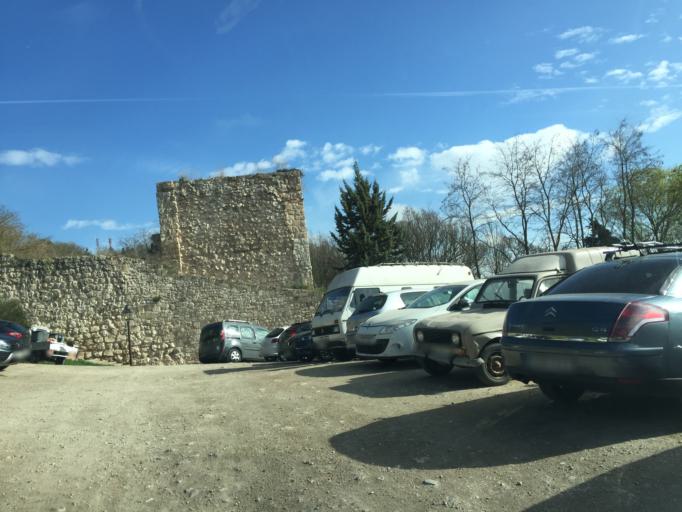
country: ES
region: Castille and Leon
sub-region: Provincia de Burgos
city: Burgos
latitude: 42.3435
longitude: -3.7055
